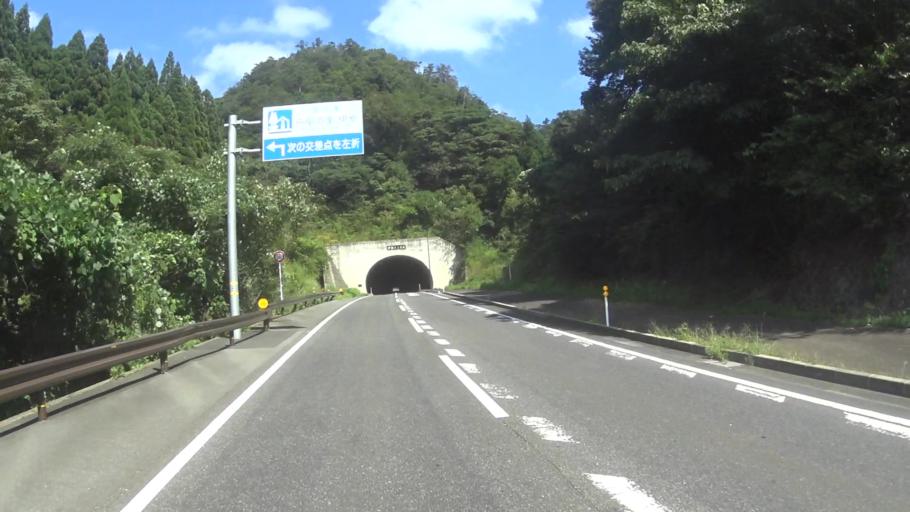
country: JP
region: Kyoto
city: Miyazu
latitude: 35.6770
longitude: 135.2759
